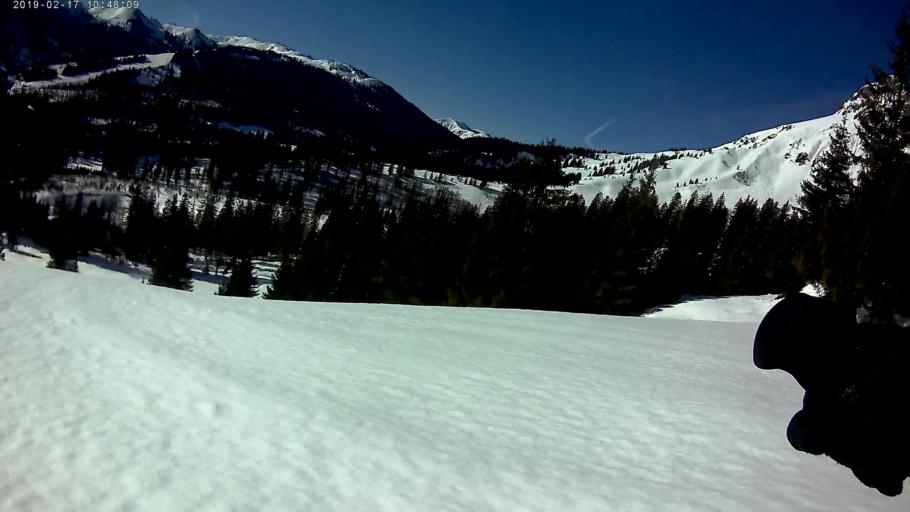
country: AT
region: Salzburg
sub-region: Politischer Bezirk Sankt Johann im Pongau
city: Muhlbach am Hochkonig
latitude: 47.4000
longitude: 13.0790
